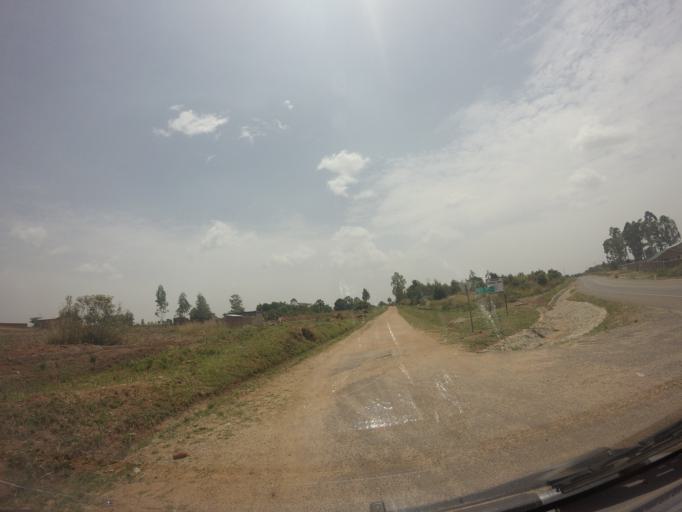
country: UG
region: Northern Region
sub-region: Arua District
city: Arua
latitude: 2.9531
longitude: 30.9144
